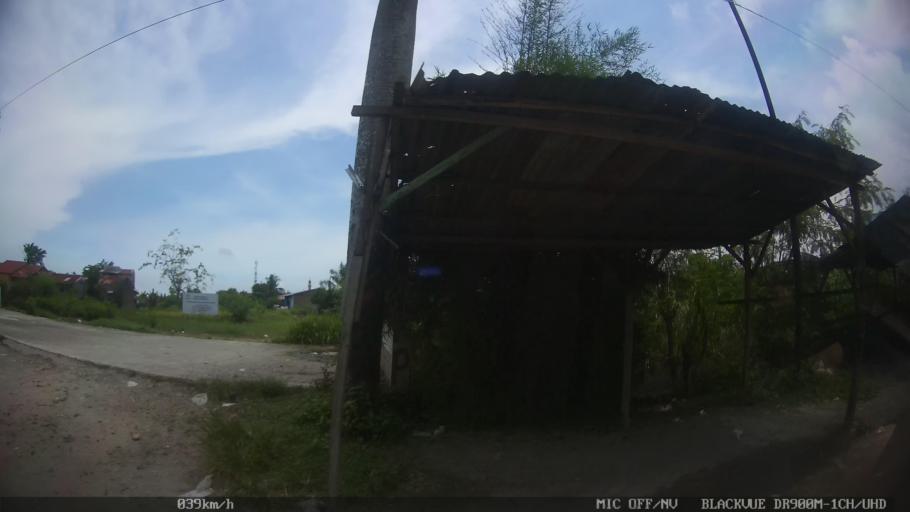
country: ID
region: North Sumatra
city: Labuhan Deli
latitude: 3.6907
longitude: 98.6942
